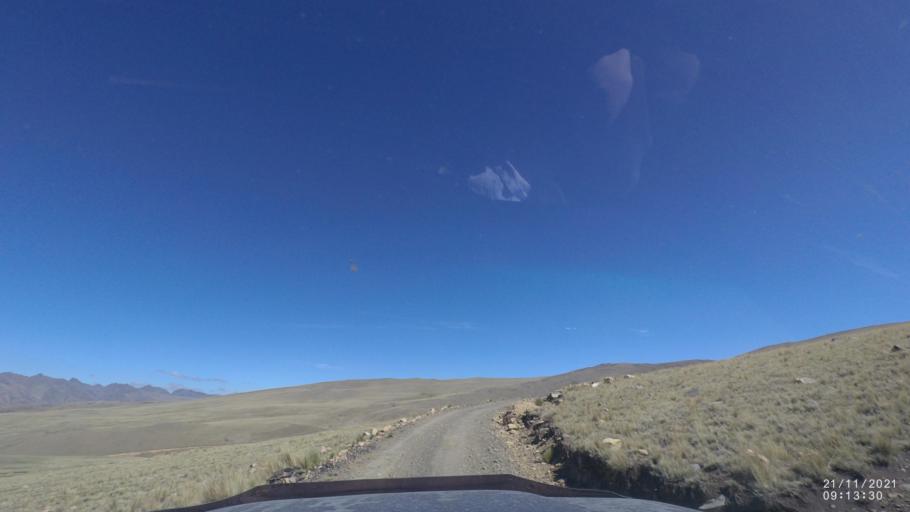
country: BO
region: Cochabamba
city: Cochabamba
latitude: -17.1404
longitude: -66.2578
